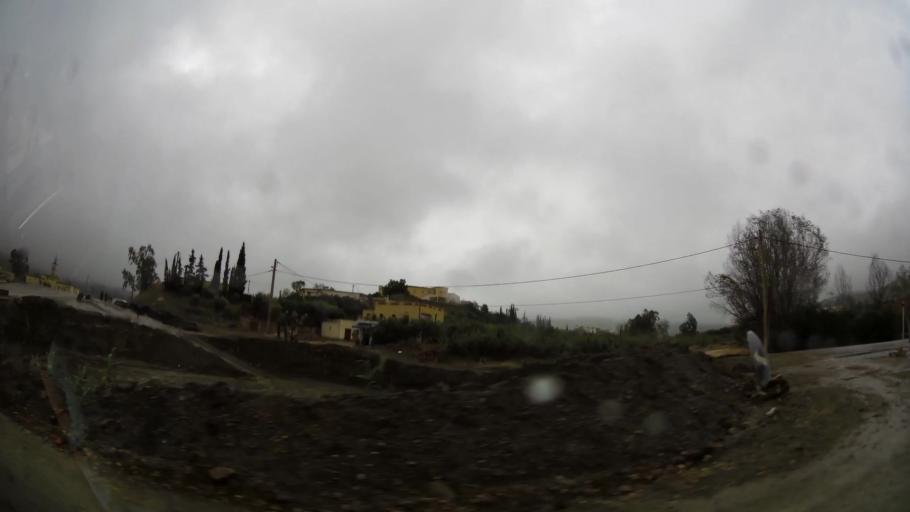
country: MA
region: Taza-Al Hoceima-Taounate
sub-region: Taza
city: Aknoul
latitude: 34.8097
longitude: -3.7357
